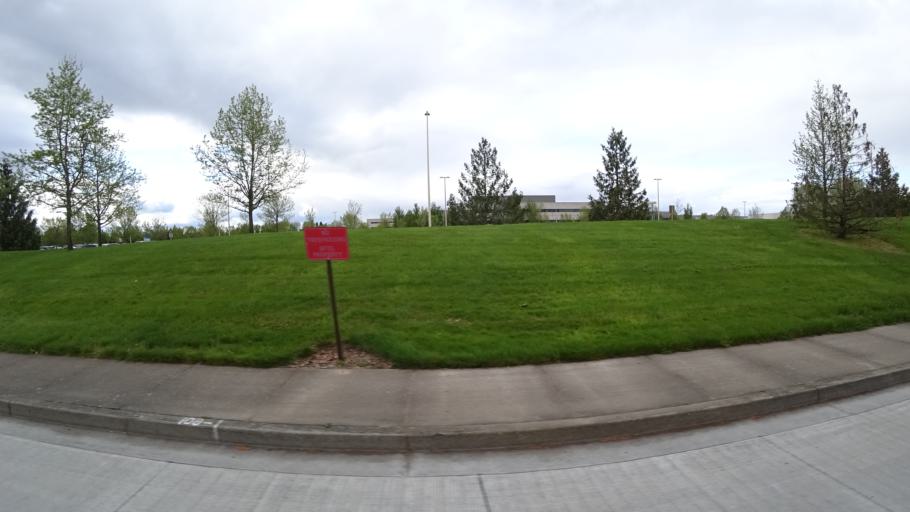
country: US
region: Oregon
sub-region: Washington County
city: Hillsboro
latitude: 45.5401
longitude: -122.9632
